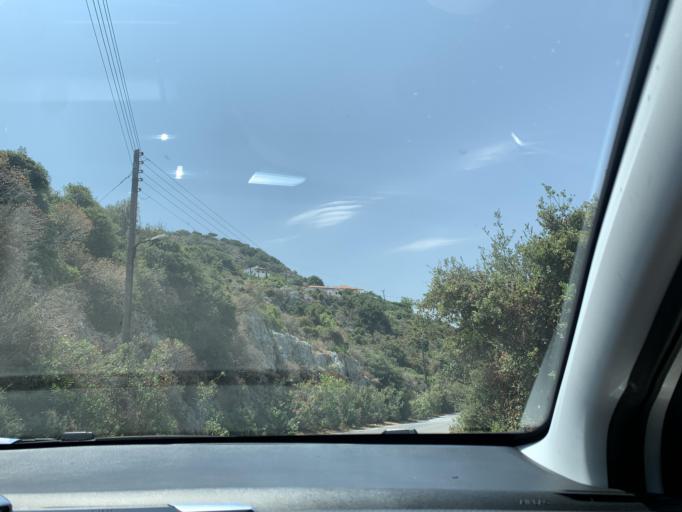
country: GR
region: Crete
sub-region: Nomos Chanias
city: Kalivai
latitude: 35.4501
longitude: 24.2075
